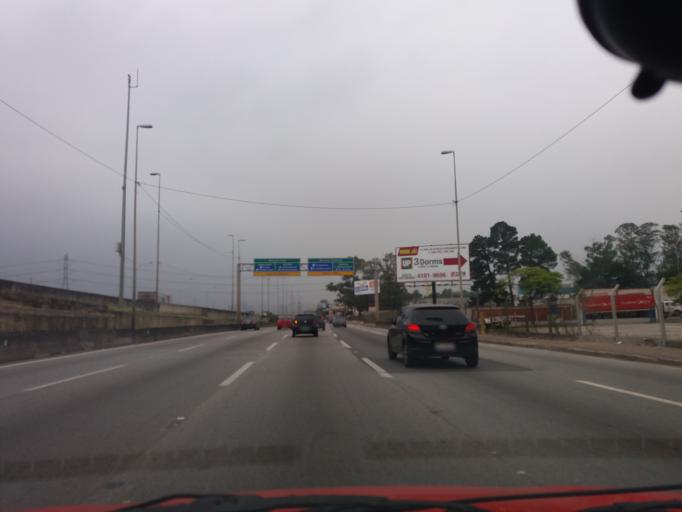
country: BR
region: Sao Paulo
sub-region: Osasco
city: Osasco
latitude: -23.5225
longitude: -46.7655
